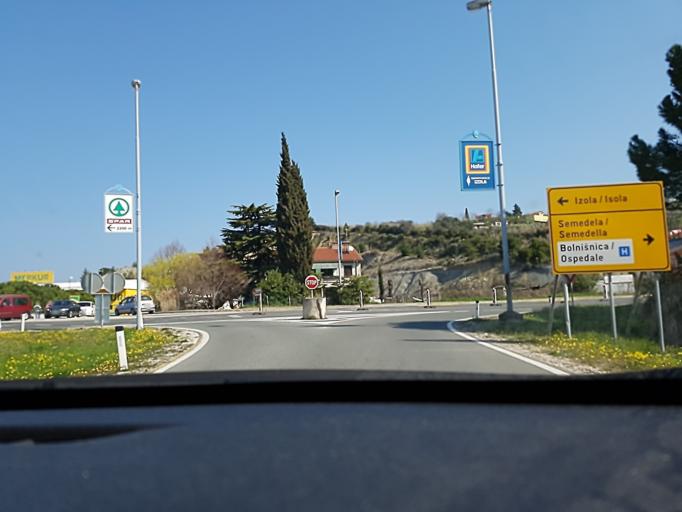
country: SI
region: Izola-Isola
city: Izola
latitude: 45.5414
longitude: 13.6772
